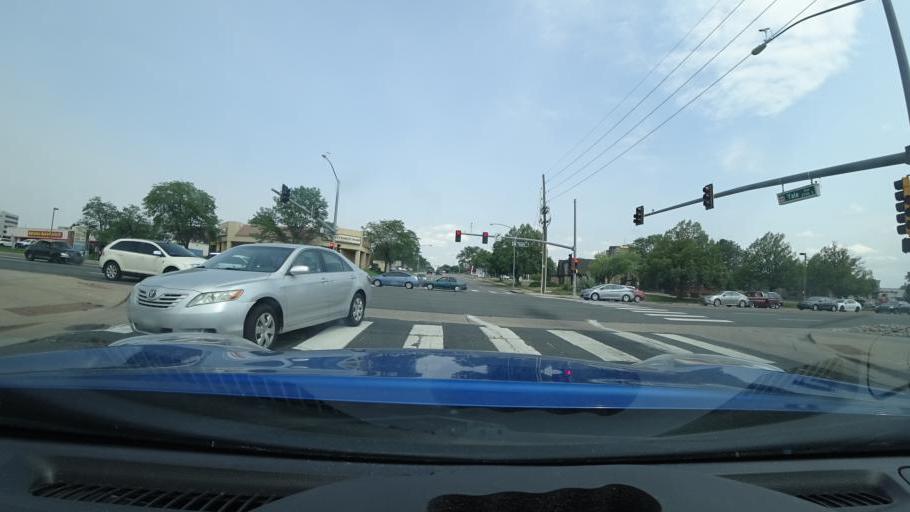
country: US
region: Colorado
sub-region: Adams County
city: Aurora
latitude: 39.6676
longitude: -104.8665
